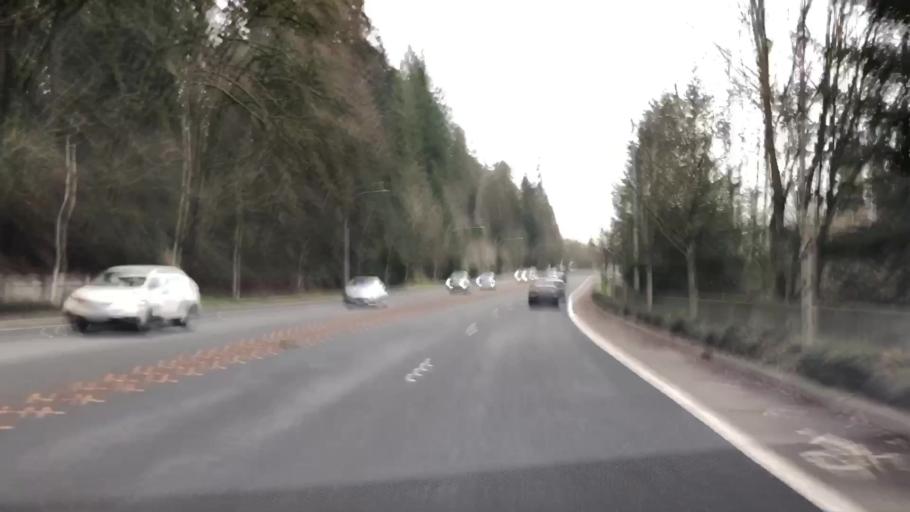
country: US
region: Washington
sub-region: King County
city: Redmond
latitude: 47.6624
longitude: -122.1264
